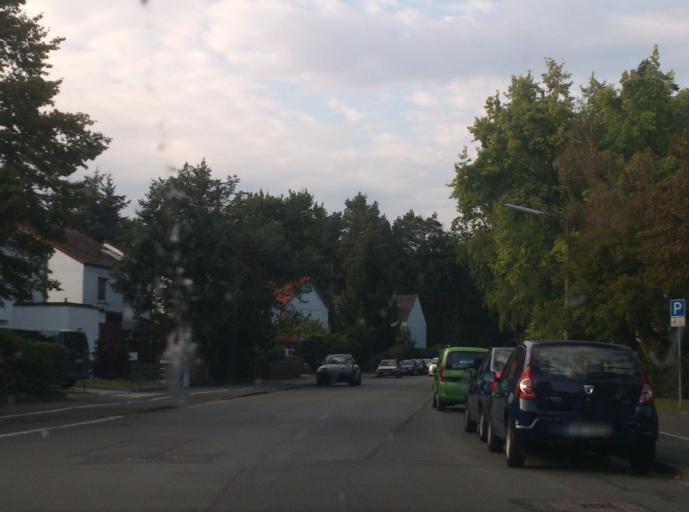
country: DE
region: Bavaria
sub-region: Regierungsbezirk Mittelfranken
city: Buckenhof
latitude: 49.6019
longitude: 11.0372
